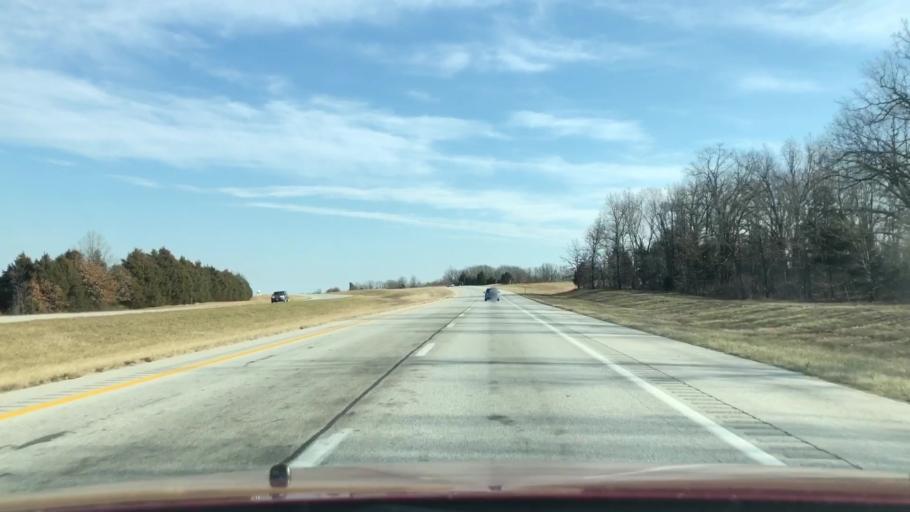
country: US
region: Missouri
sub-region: Webster County
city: Seymour
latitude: 37.1651
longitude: -92.8769
